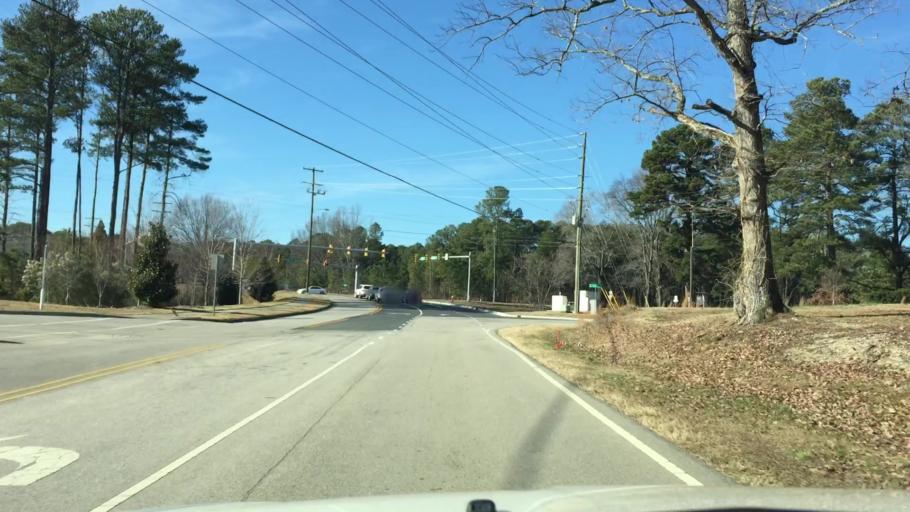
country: US
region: North Carolina
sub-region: Wake County
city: Green Level
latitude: 35.7605
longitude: -78.8743
